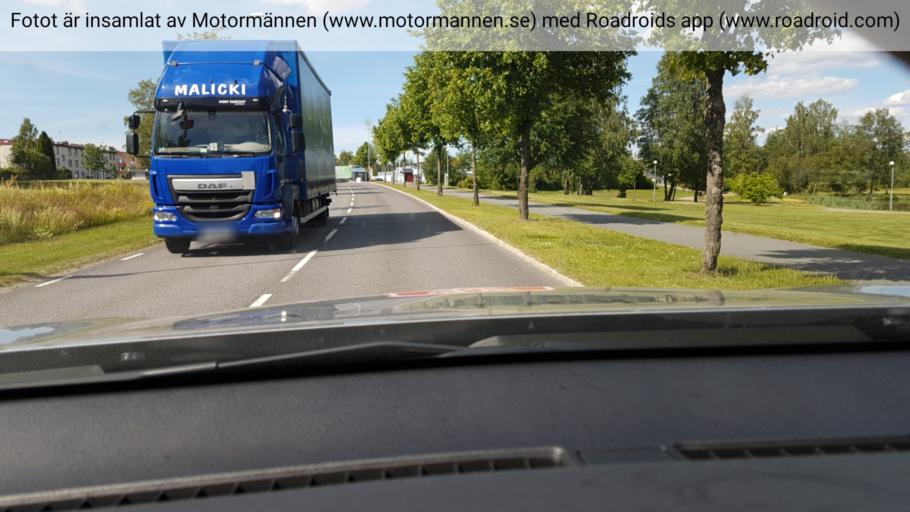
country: SE
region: Joenkoeping
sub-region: Vaggeryds Kommun
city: Vaggeryd
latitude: 57.5037
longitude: 14.1432
